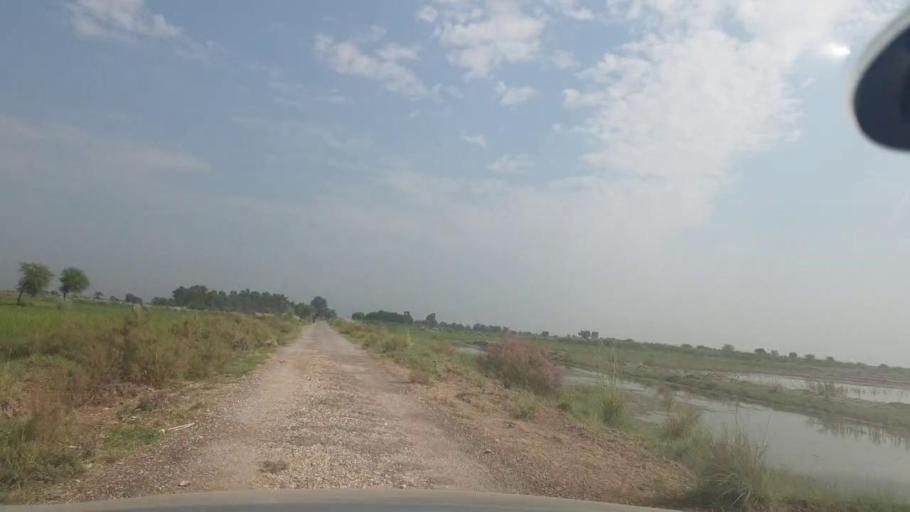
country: PK
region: Balochistan
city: Mehrabpur
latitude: 28.0484
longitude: 68.1226
